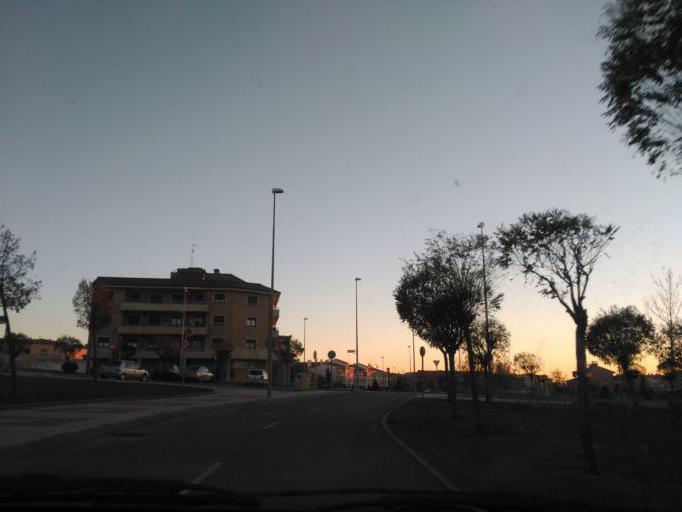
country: ES
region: Castille and Leon
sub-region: Provincia de Salamanca
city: Carbajosa de la Sagrada
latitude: 40.9366
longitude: -5.6499
